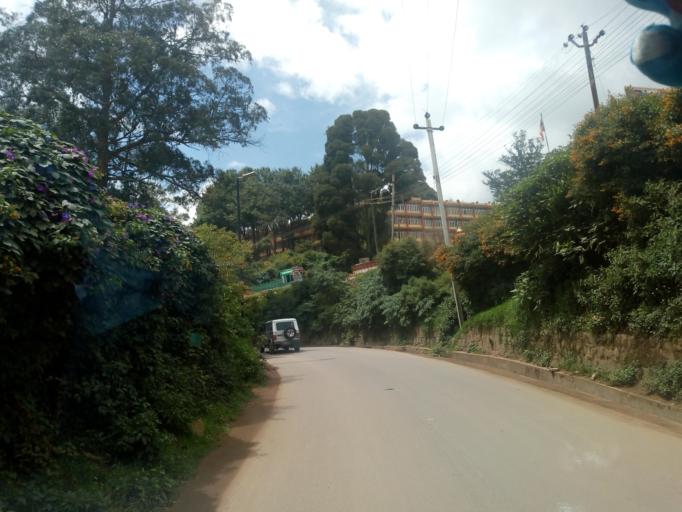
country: IN
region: Tamil Nadu
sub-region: Nilgiri
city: Ooty
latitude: 11.4018
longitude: 76.6979
